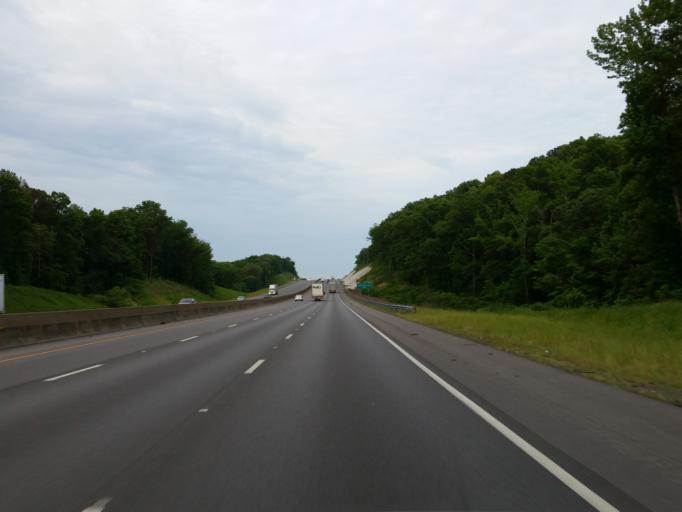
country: US
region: Alabama
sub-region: Saint Clair County
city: Moody
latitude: 33.5933
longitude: -86.4154
